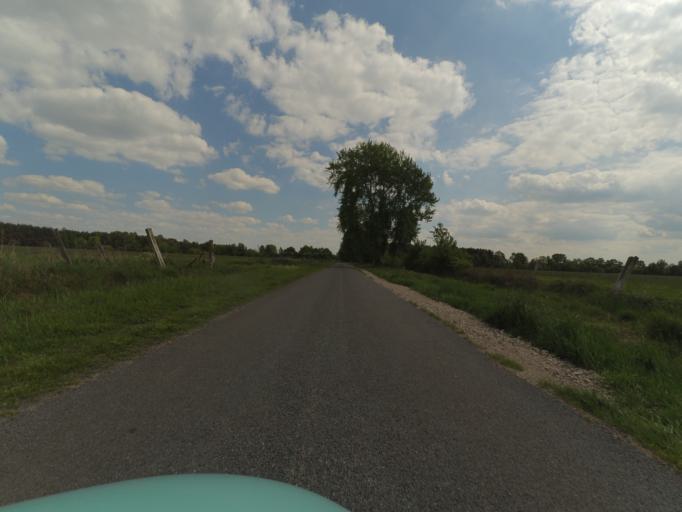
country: DE
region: Lower Saxony
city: Adelheidsdorf
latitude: 52.5701
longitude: 10.0189
